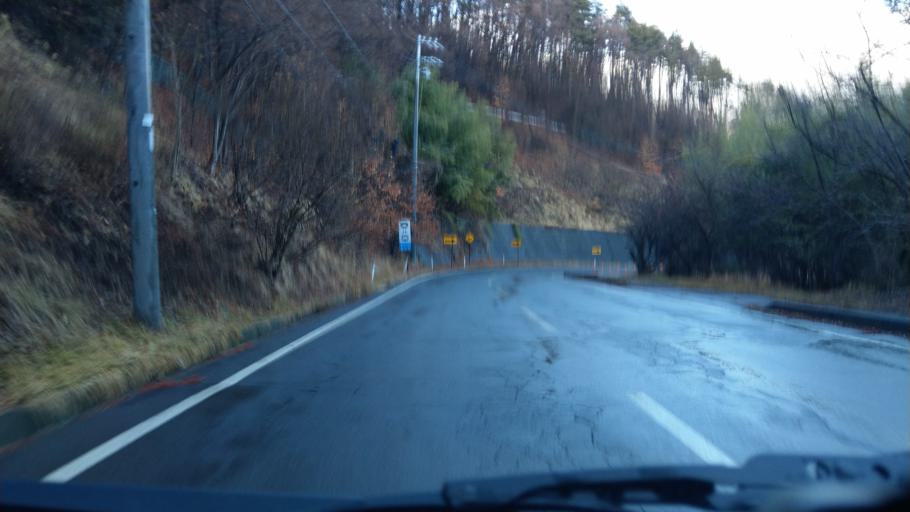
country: JP
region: Nagano
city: Komoro
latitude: 36.3001
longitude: 138.4137
